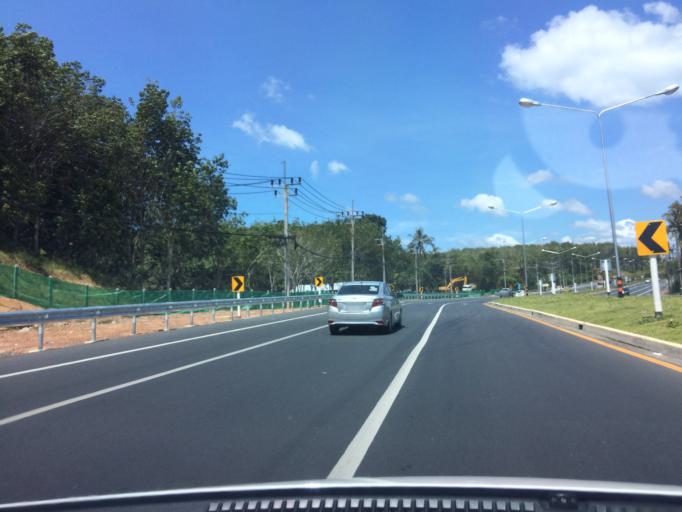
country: TH
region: Phuket
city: Thalang
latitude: 8.1389
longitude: 98.3413
